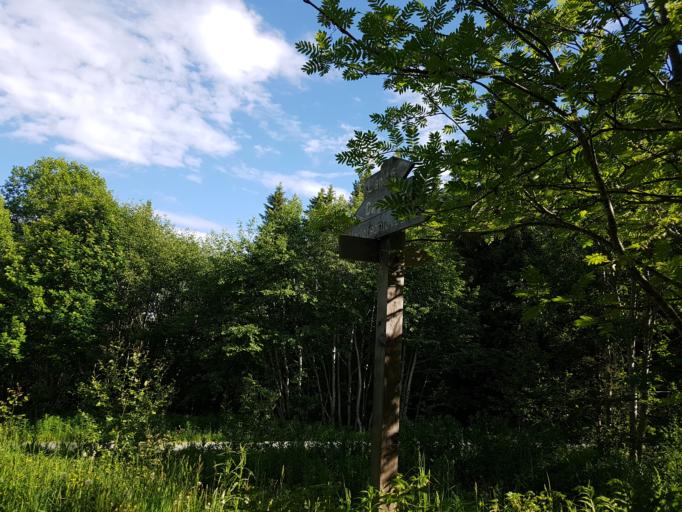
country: NO
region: Sor-Trondelag
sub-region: Trondheim
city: Trondheim
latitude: 63.3968
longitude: 10.3249
